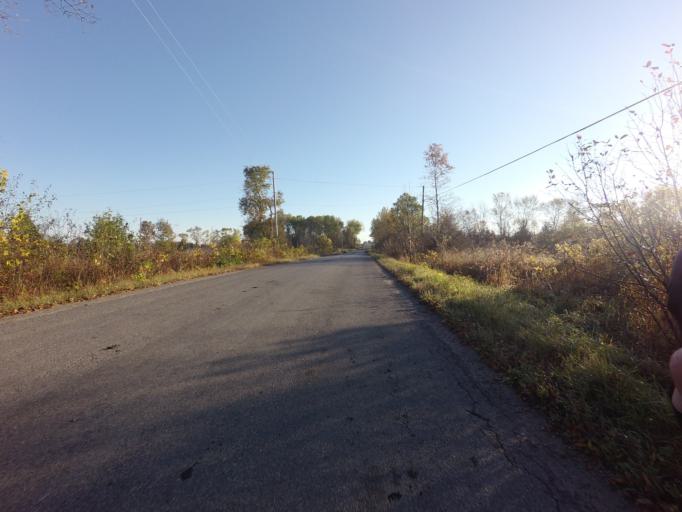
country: CA
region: Ontario
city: Quinte West
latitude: 44.0228
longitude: -77.4917
